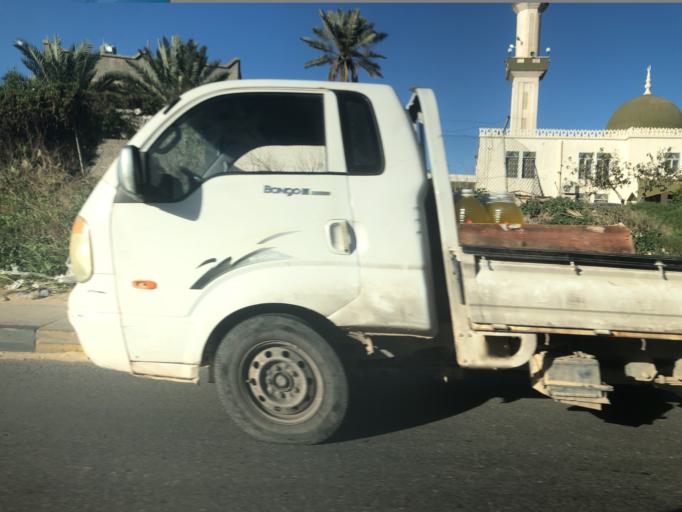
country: LY
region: Tripoli
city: Tripoli
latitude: 32.8689
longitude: 13.2542
